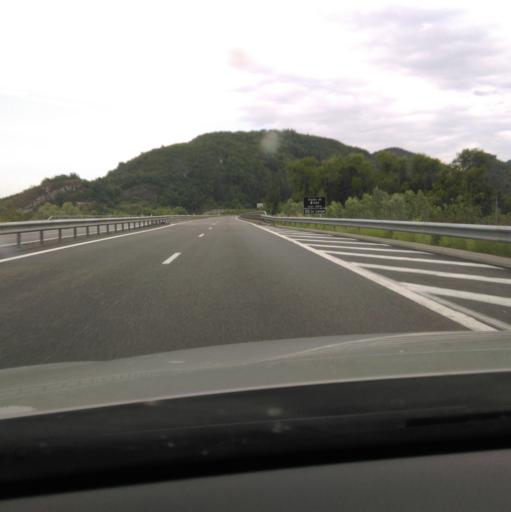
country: FR
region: Rhone-Alpes
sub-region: Departement de l'Ain
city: Montreal-la-Cluse
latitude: 46.1727
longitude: 5.5606
